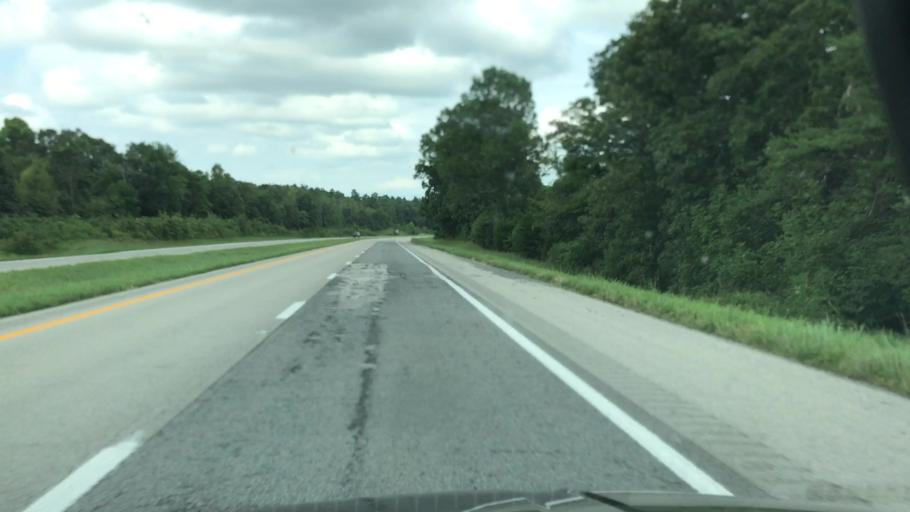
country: US
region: Kentucky
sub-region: Caldwell County
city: Princeton
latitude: 37.1493
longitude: -87.7962
